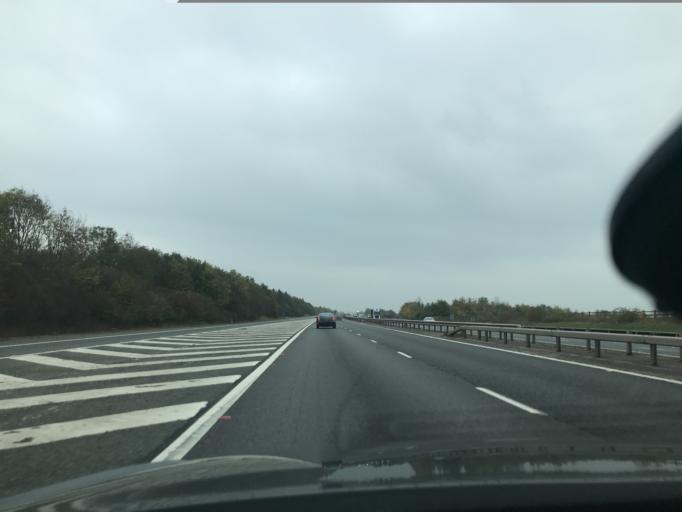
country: GB
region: England
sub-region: Oxfordshire
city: Bicester
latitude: 51.8653
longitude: -1.1937
